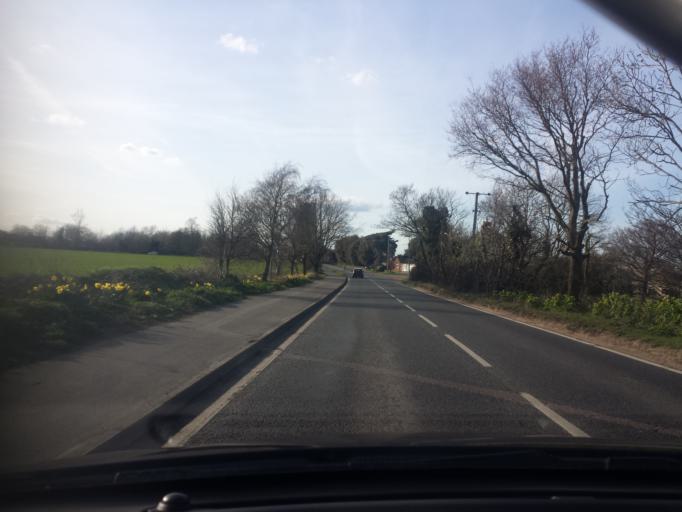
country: GB
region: England
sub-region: Essex
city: Brightlingsea
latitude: 51.8267
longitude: 1.0160
